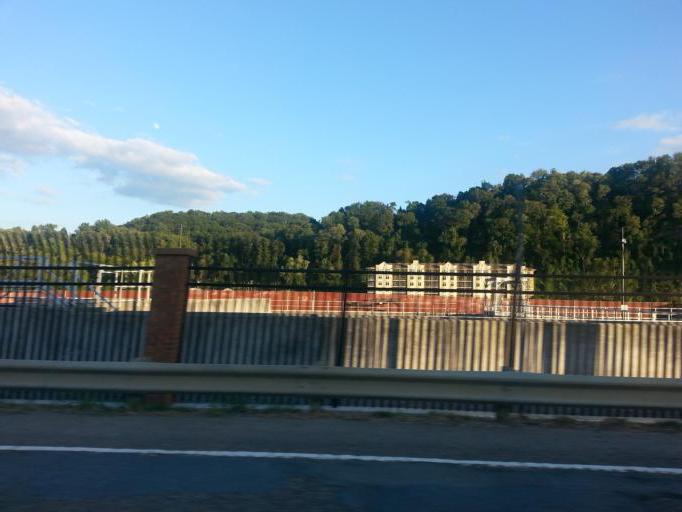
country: US
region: Tennessee
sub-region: Knox County
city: Knoxville
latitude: 35.9453
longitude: -83.9274
